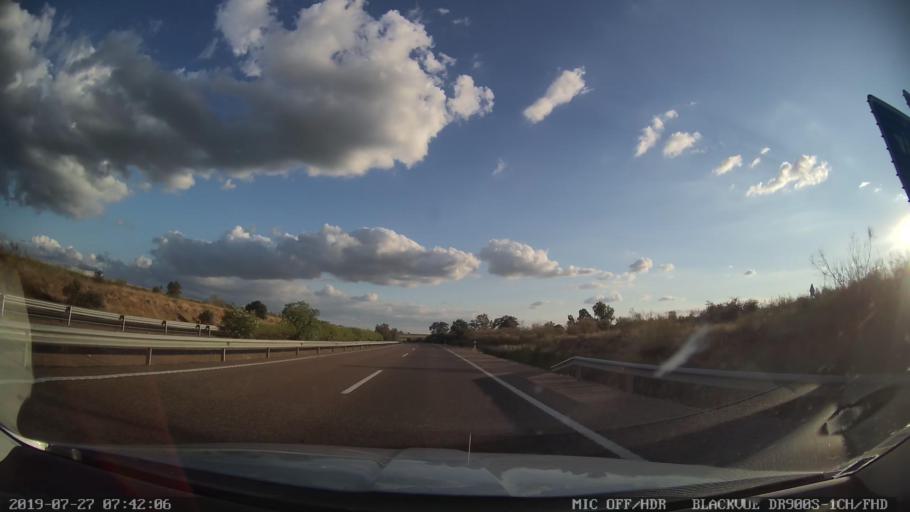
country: ES
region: Extremadura
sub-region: Provincia de Badajoz
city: Santa Amalia
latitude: 39.0195
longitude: -6.0834
